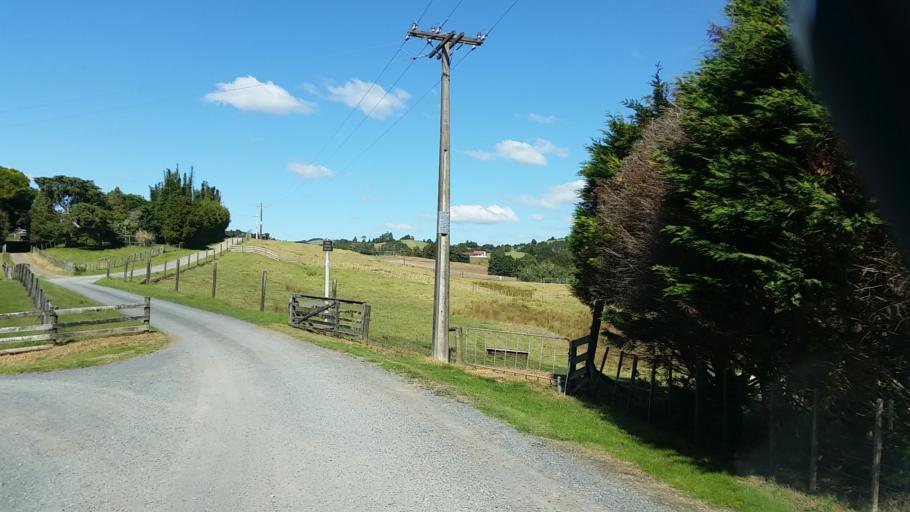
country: NZ
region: Northland
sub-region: Whangarei
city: Maungatapere
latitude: -35.6982
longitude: 174.2291
